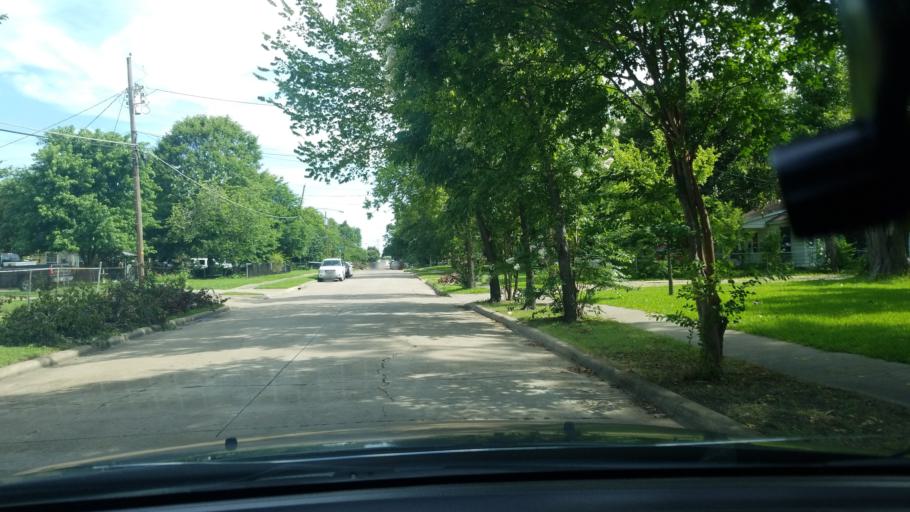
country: US
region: Texas
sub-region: Dallas County
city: Balch Springs
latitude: 32.7639
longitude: -96.6714
